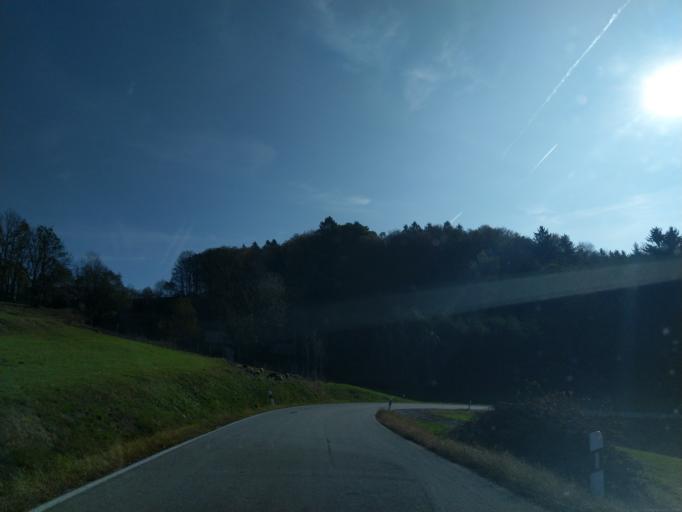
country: DE
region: Bavaria
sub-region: Lower Bavaria
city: Grattersdorf
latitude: 48.7996
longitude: 13.1880
